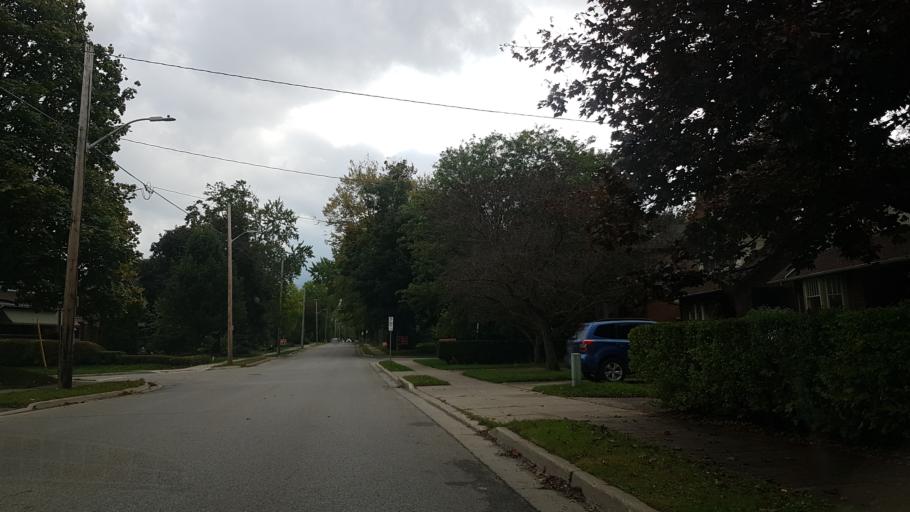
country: CA
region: Ontario
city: London
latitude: 42.9640
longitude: -81.2483
